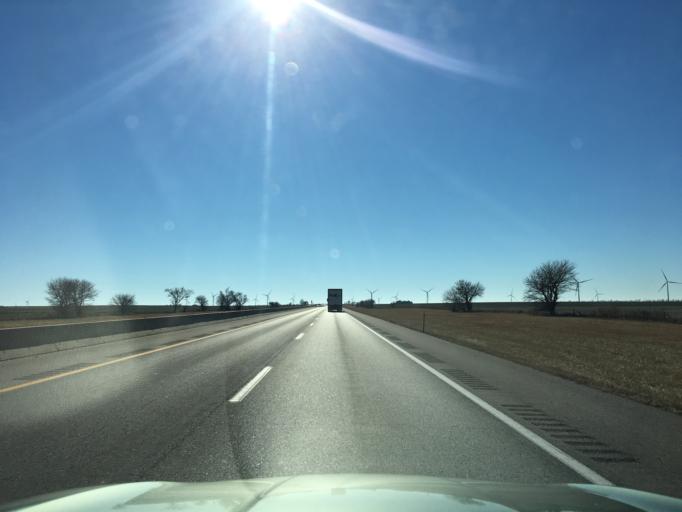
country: US
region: Kansas
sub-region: Sumner County
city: Wellington
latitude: 37.1749
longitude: -97.3396
